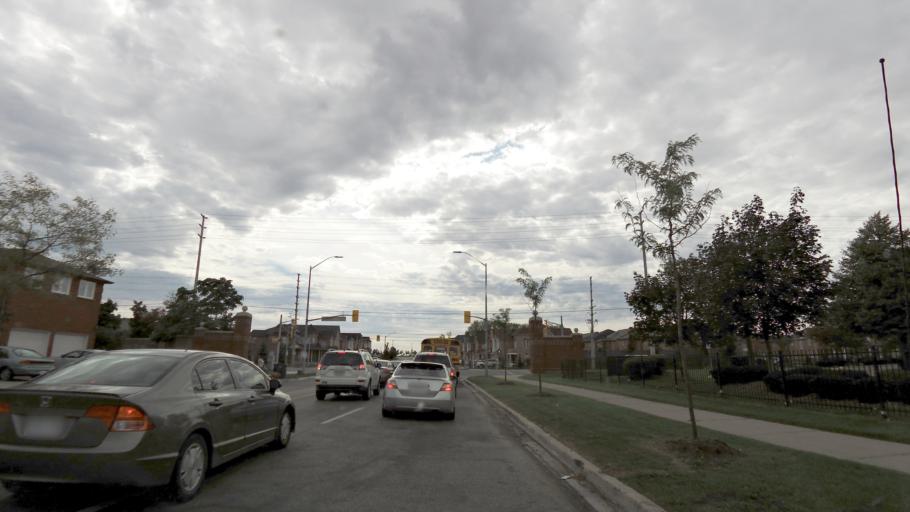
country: CA
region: Ontario
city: Mississauga
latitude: 43.5907
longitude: -79.6658
